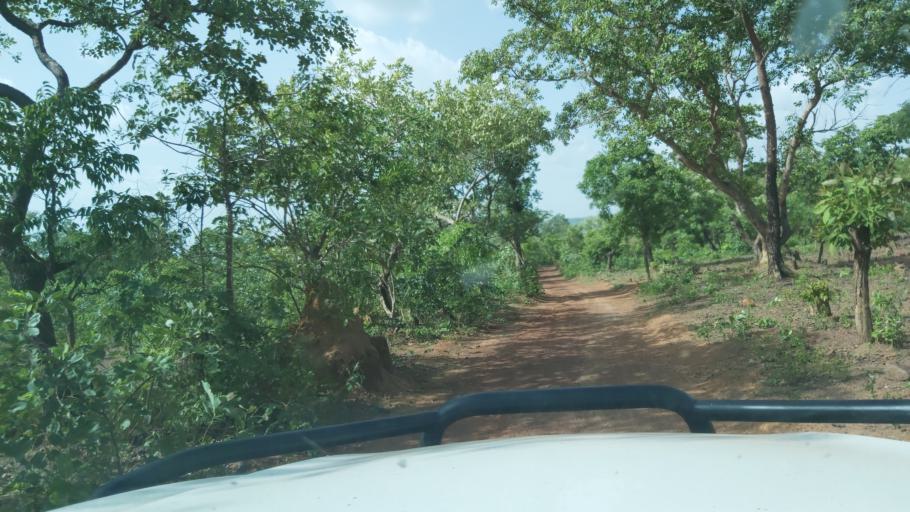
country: ML
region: Koulikoro
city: Kangaba
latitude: 12.4032
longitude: -8.8861
